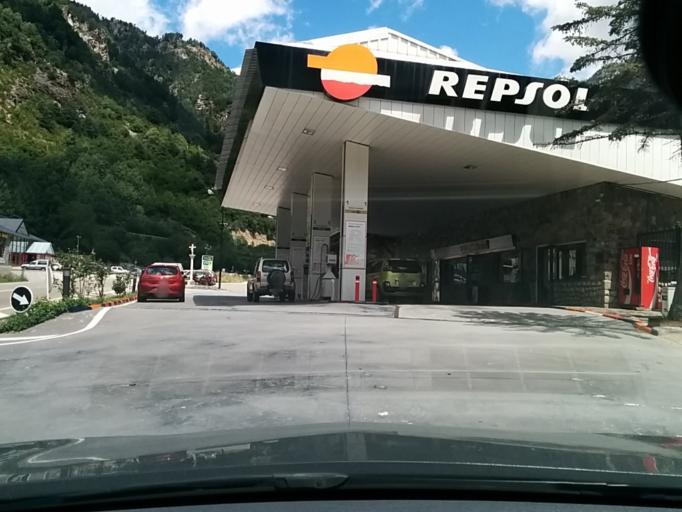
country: ES
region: Aragon
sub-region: Provincia de Huesca
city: Bielsa
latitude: 42.6610
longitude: 0.2094
